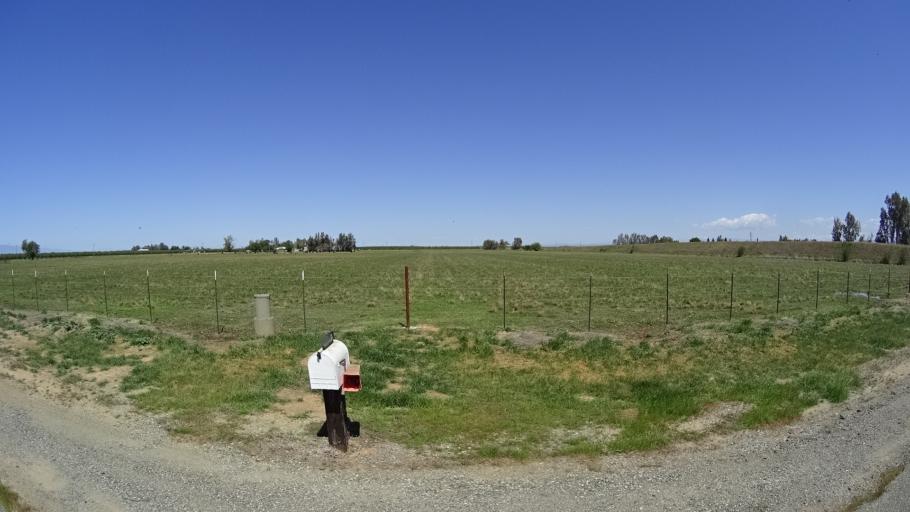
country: US
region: California
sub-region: Glenn County
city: Orland
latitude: 39.7977
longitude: -122.1572
